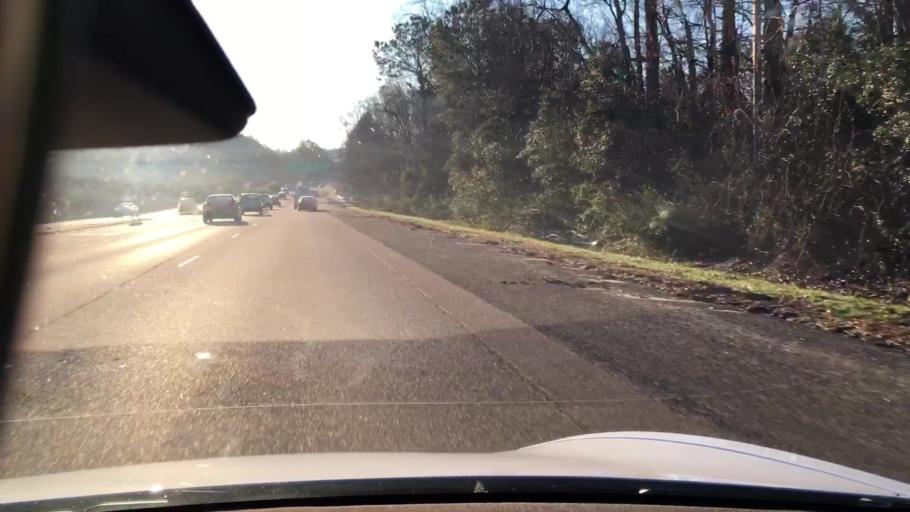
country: US
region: Virginia
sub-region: Chesterfield County
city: Bon Air
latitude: 37.5408
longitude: -77.5335
